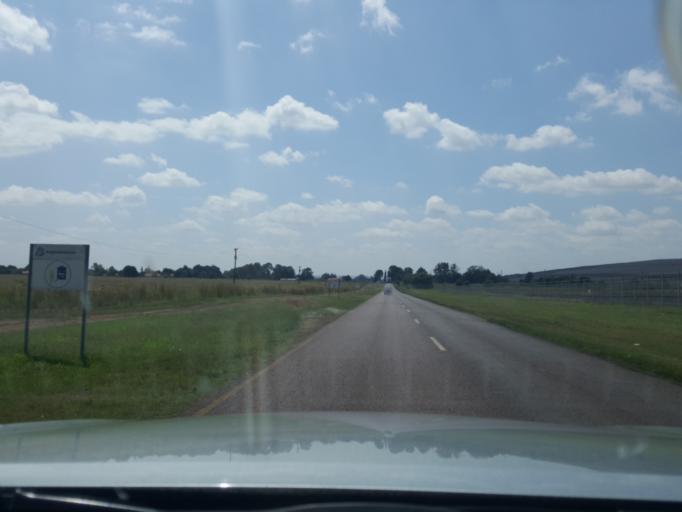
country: ZA
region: Mpumalanga
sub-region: Nkangala District Municipality
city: Middelburg
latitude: -25.9776
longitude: 29.4513
